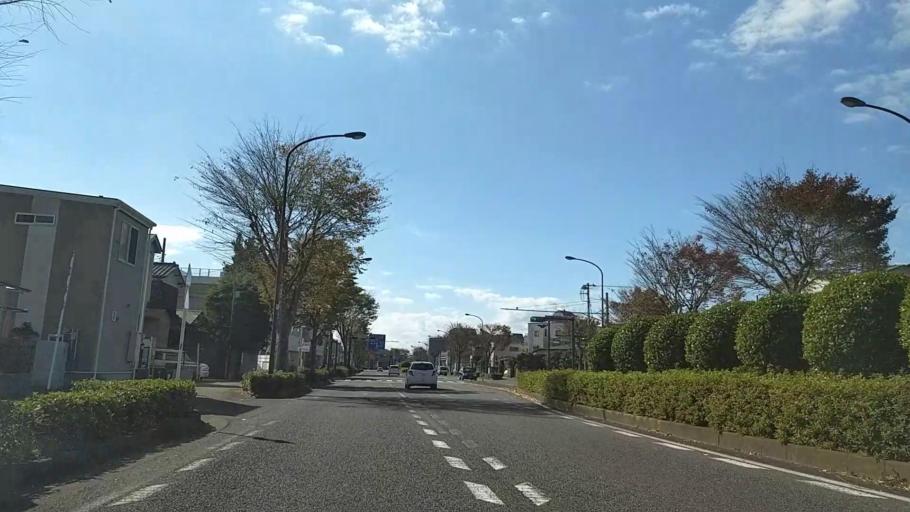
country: JP
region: Kanagawa
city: Hiratsuka
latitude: 35.3275
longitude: 139.3332
